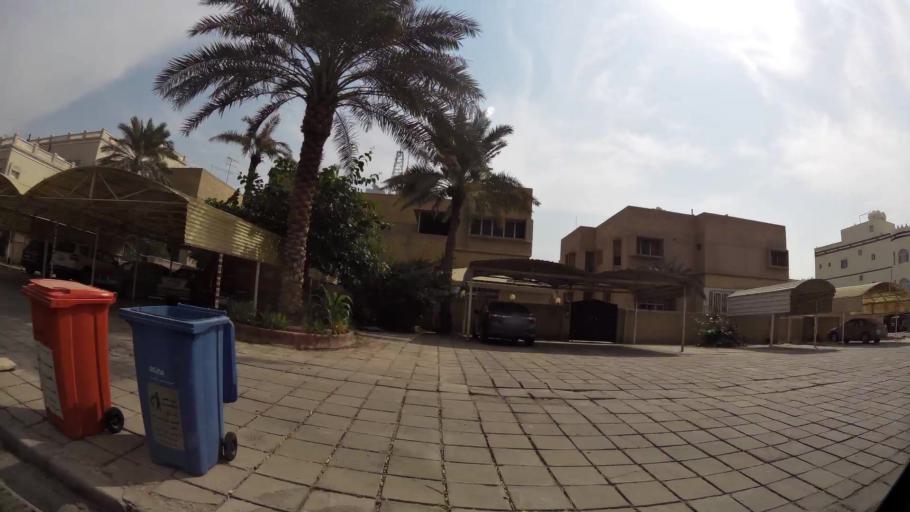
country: KW
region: Al Asimah
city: Ad Dasmah
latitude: 29.3420
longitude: 47.9953
